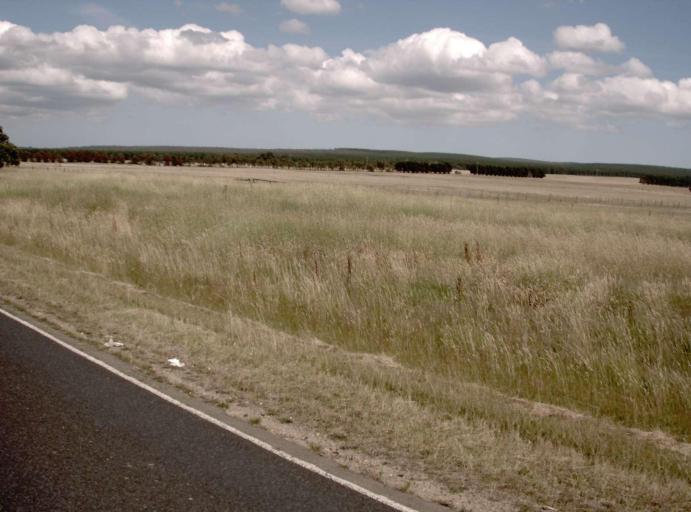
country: AU
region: Victoria
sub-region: Wellington
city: Heyfield
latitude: -38.1551
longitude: 146.8405
